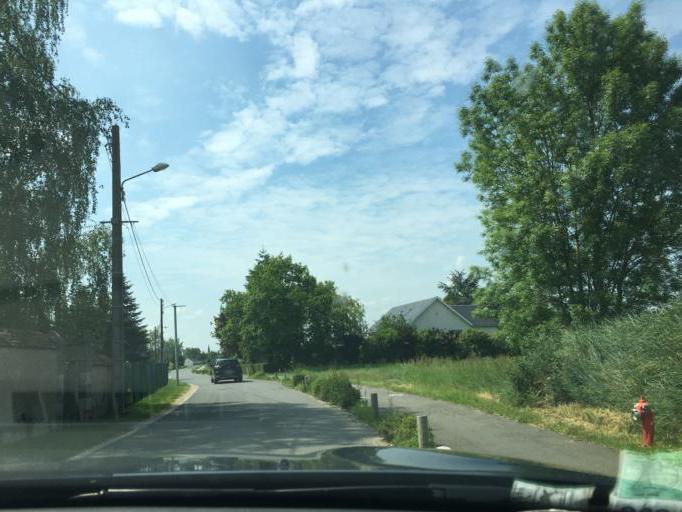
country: FR
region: Centre
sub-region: Departement du Loiret
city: Saint-Denis-en-Val
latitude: 47.8876
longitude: 1.9598
